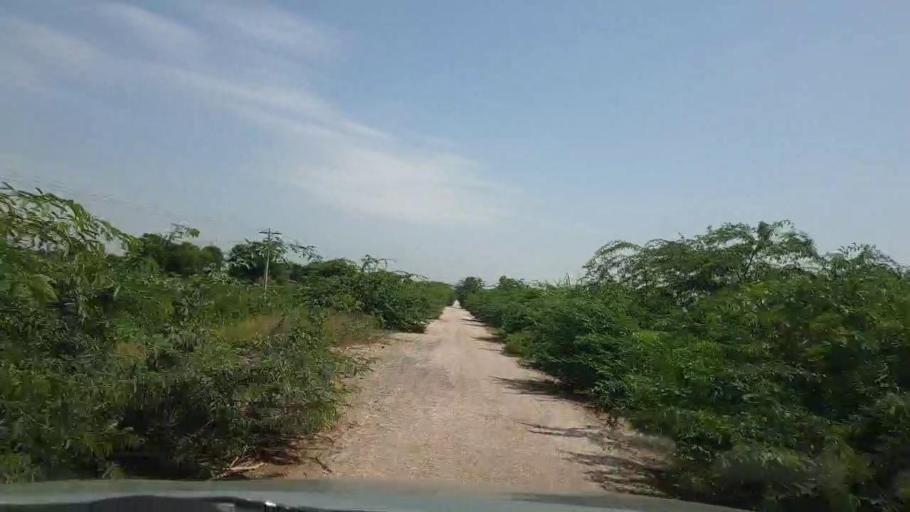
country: PK
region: Sindh
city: Bozdar
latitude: 27.0981
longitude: 68.9740
